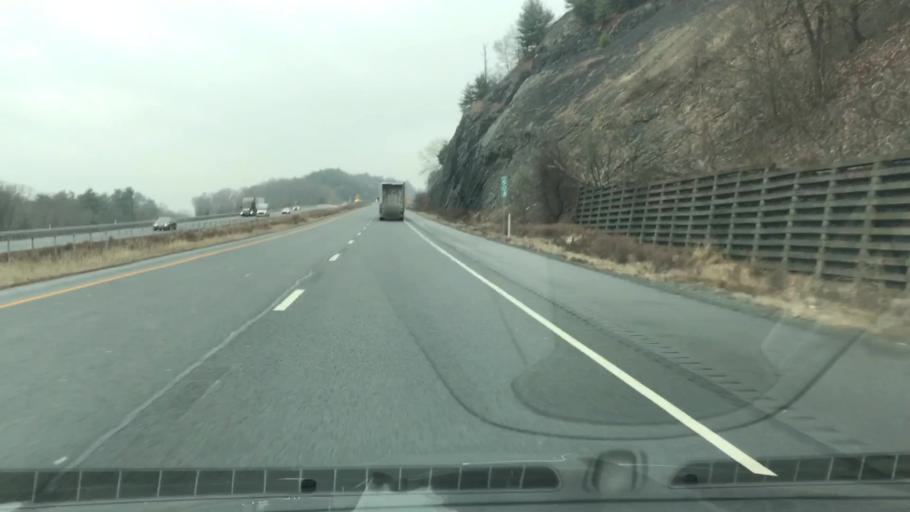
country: US
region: Pennsylvania
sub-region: Pike County
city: Milford
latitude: 41.3462
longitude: -74.7570
